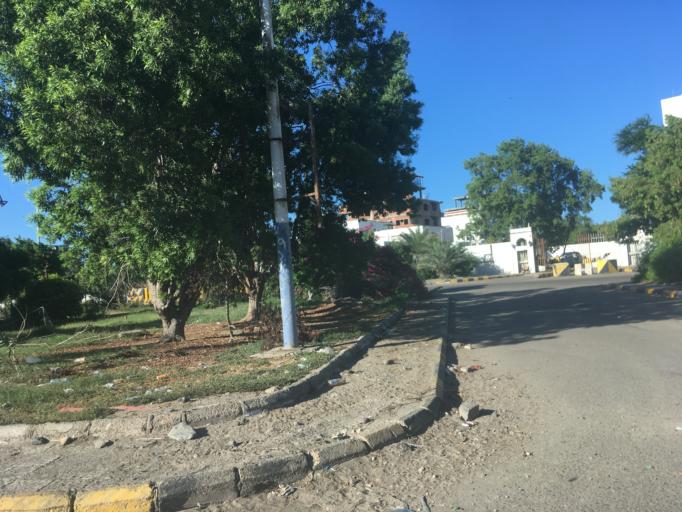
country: YE
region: Aden
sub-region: Craiter
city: Aden
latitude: 12.7920
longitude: 45.0379
